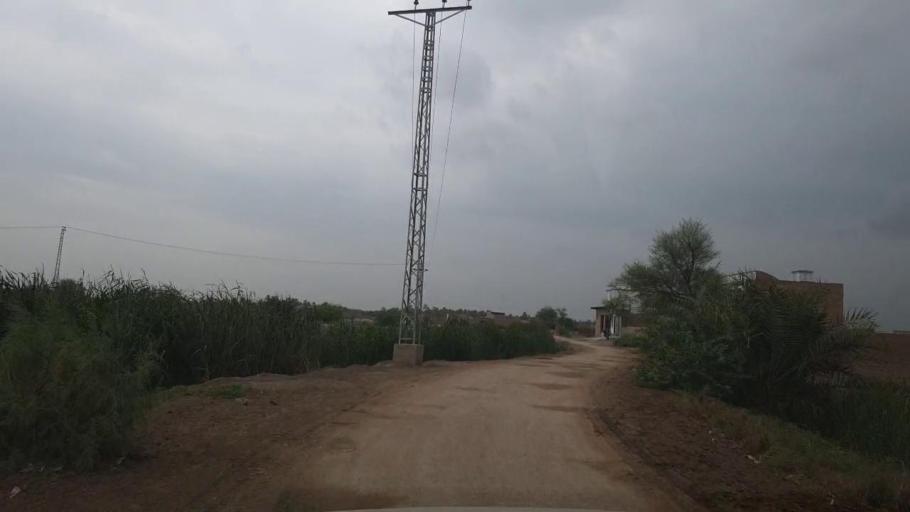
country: PK
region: Sindh
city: Khairpur
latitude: 27.5335
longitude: 68.7331
